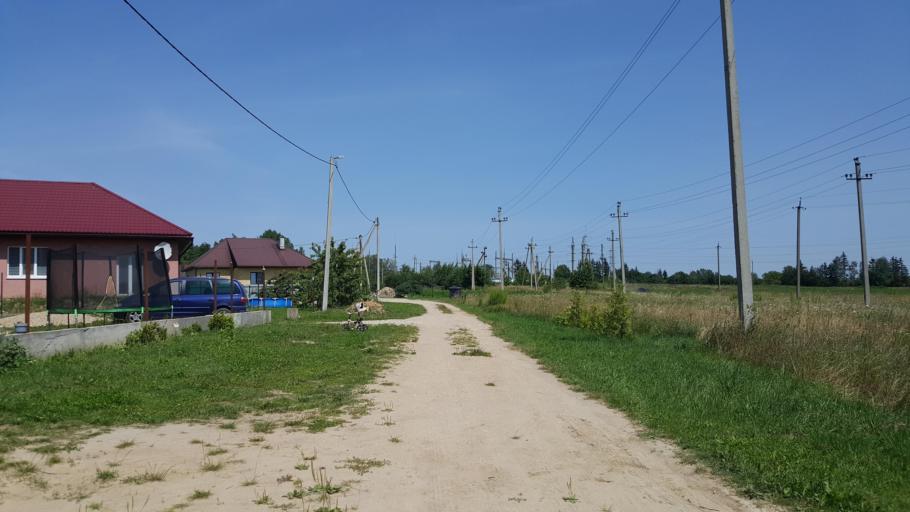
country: BY
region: Brest
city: Vysokaye
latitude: 52.3596
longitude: 23.3926
